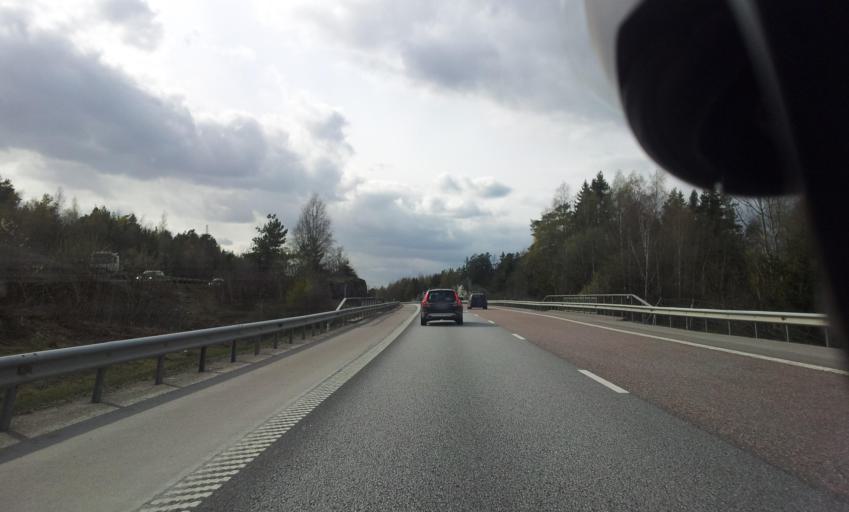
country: SE
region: Uppsala
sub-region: Habo Kommun
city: Balsta
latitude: 59.5922
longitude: 17.4885
